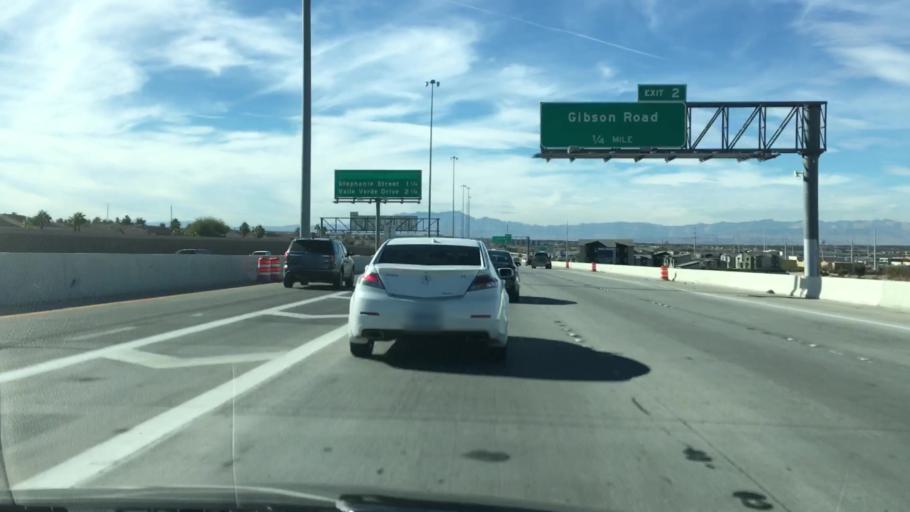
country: US
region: Nevada
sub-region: Clark County
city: Henderson
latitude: 36.0331
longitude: -115.0204
